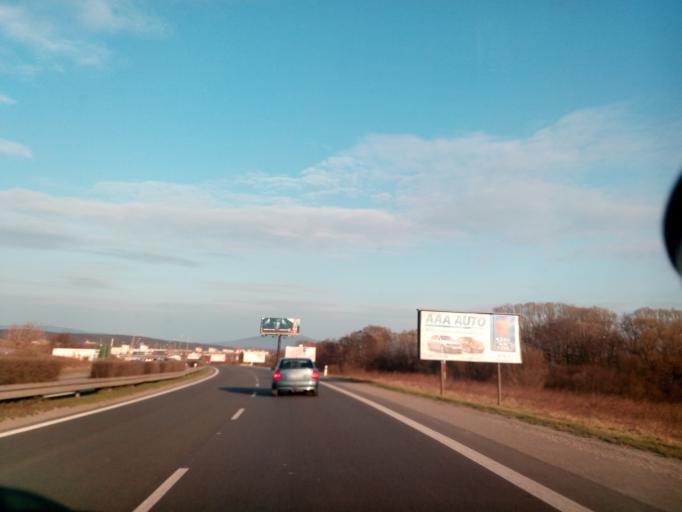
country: SK
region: Kosicky
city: Kosice
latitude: 48.6885
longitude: 21.2490
